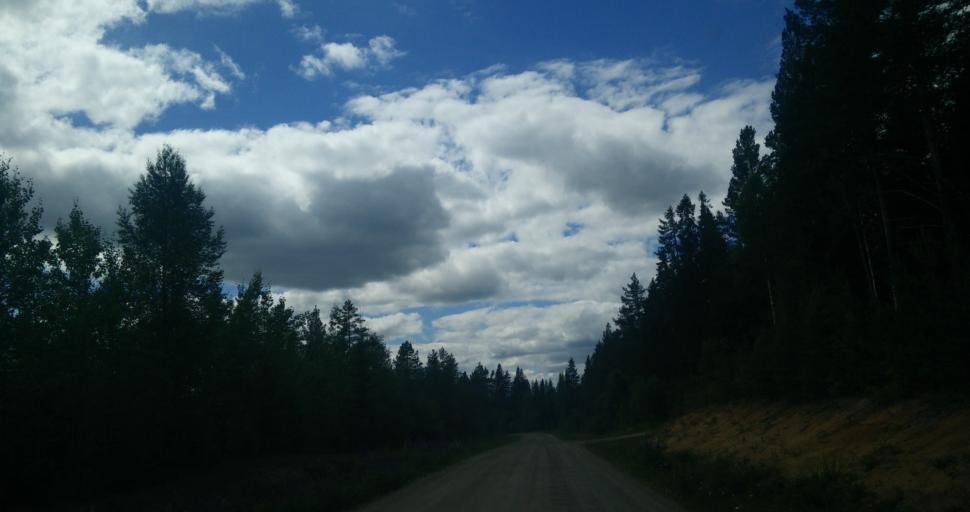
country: SE
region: Gaevleborg
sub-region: Nordanstigs Kommun
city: Bergsjoe
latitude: 62.1246
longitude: 17.1080
